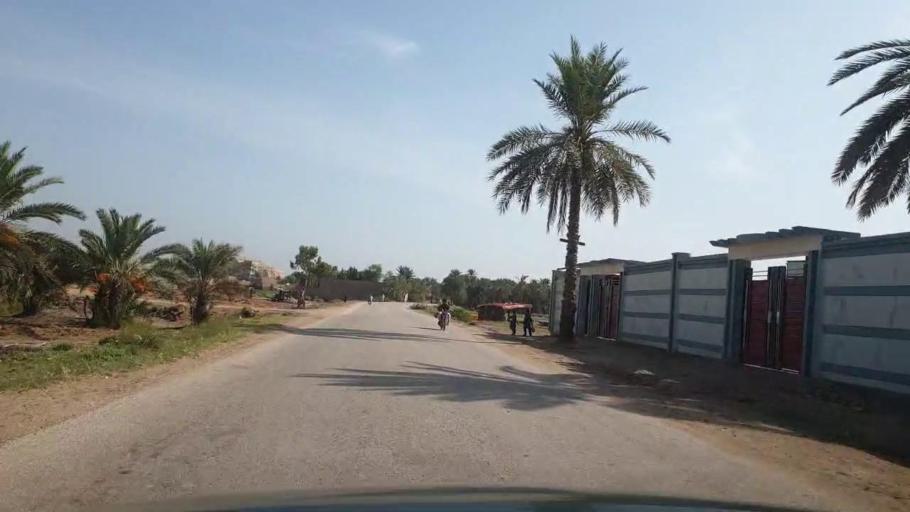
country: PK
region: Sindh
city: Rohri
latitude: 27.6725
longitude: 68.8796
